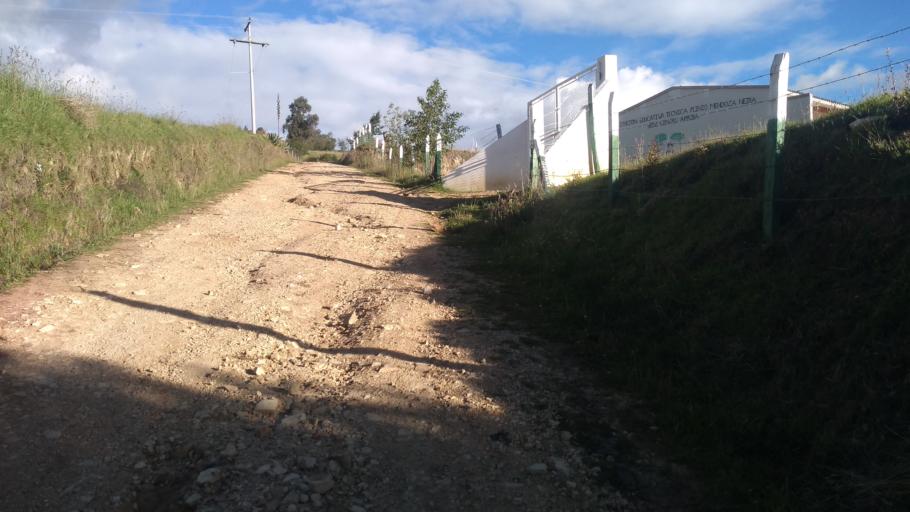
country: CO
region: Boyaca
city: Toca
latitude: 5.5602
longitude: -73.1688
